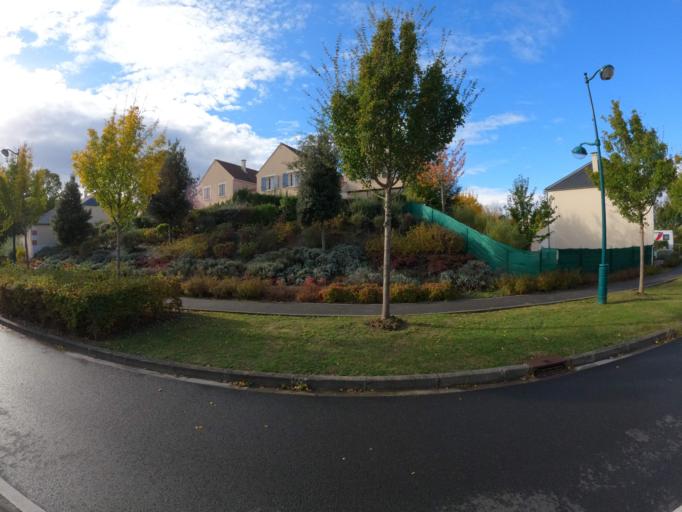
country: FR
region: Ile-de-France
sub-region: Departement de Seine-et-Marne
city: Montry
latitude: 48.8749
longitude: 2.8209
